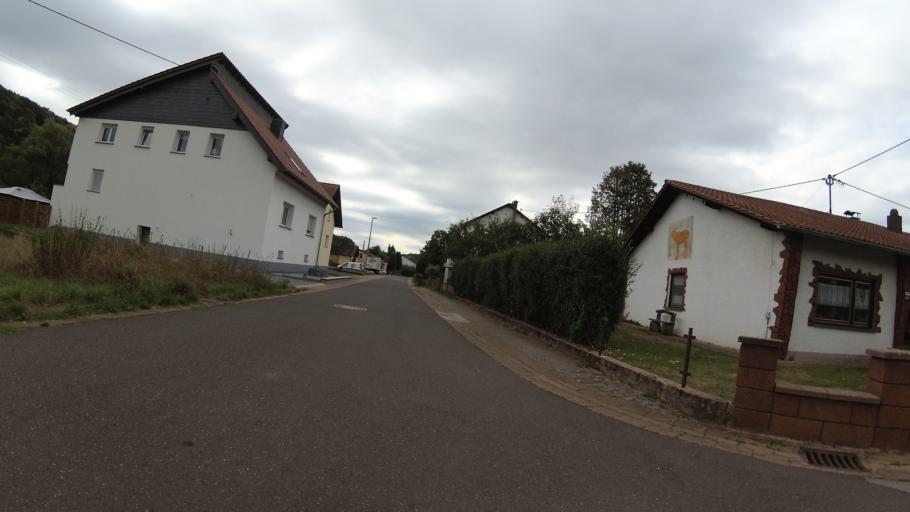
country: DE
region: Saarland
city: Wadern
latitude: 49.5086
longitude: 6.8747
